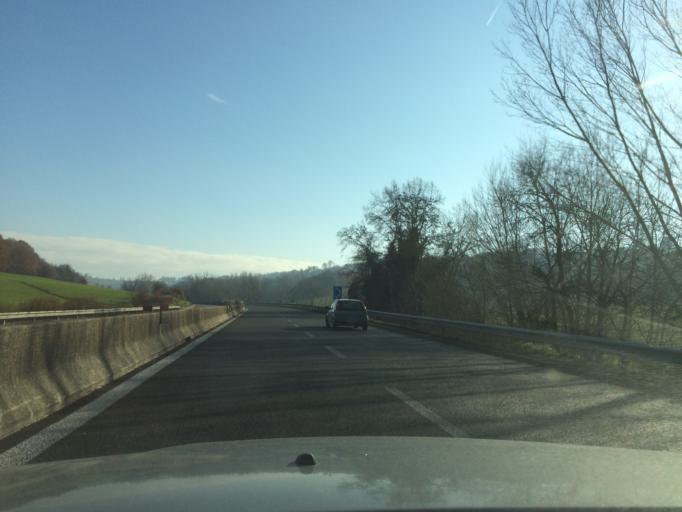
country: IT
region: Umbria
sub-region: Provincia di Perugia
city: Todi
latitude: 42.7604
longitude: 12.4564
